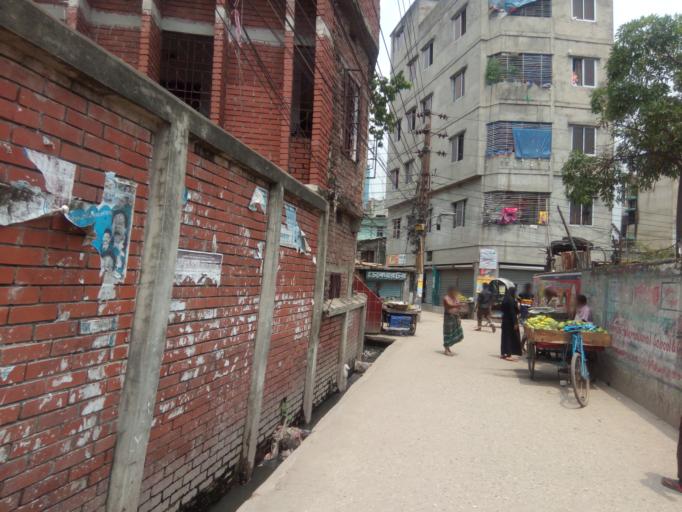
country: BD
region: Dhaka
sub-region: Dhaka
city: Dhaka
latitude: 23.6913
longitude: 90.4345
